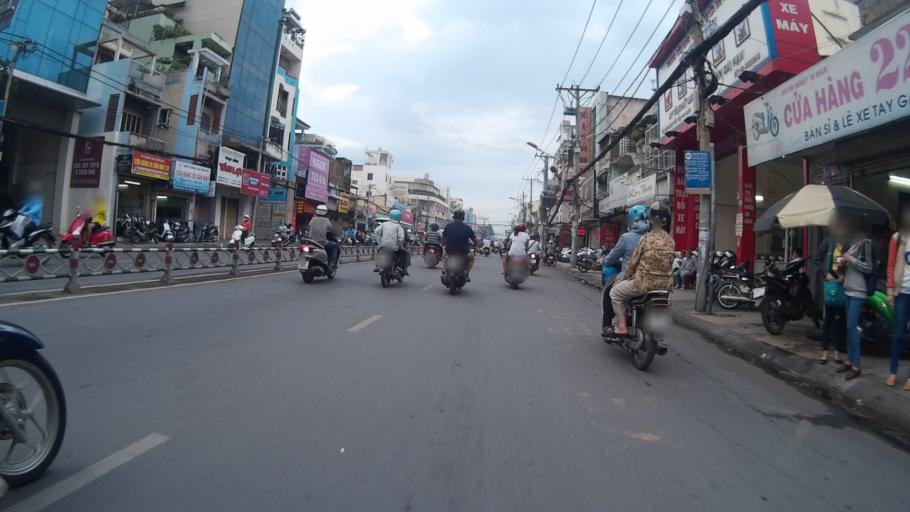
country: VN
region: Ho Chi Minh City
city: Quan Phu Nhuan
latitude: 10.7993
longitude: 106.6794
